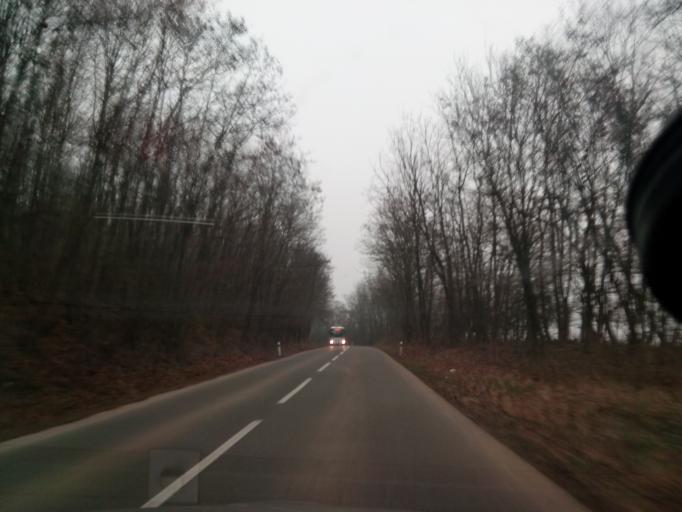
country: SK
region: Kosicky
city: Kosice
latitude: 48.6737
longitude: 21.1268
